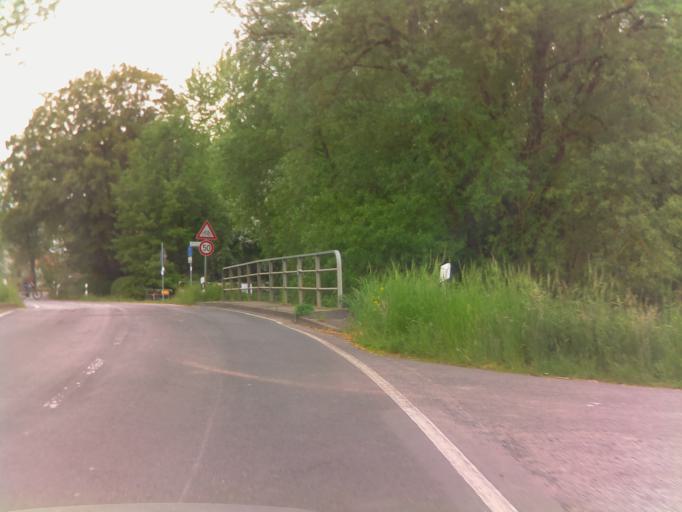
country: DE
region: Hesse
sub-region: Regierungsbezirk Kassel
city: Schrecksbach
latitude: 50.8836
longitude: 9.2583
